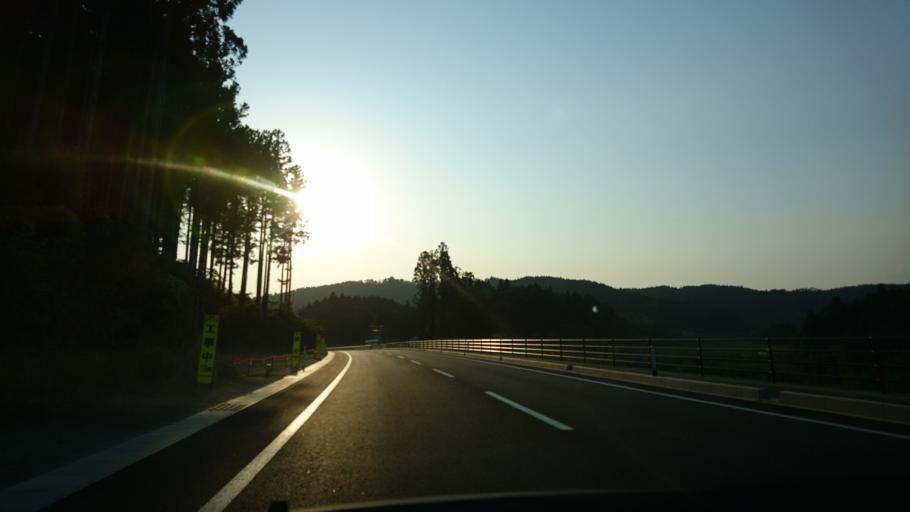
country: JP
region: Iwate
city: Ichinoseki
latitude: 38.9364
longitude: 141.4361
